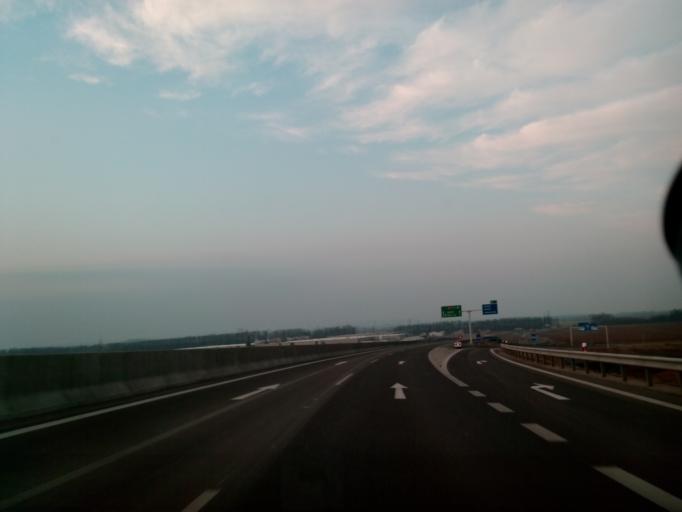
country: HU
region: Borsod-Abauj-Zemplen
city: Gonc
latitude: 48.5446
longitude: 21.2329
